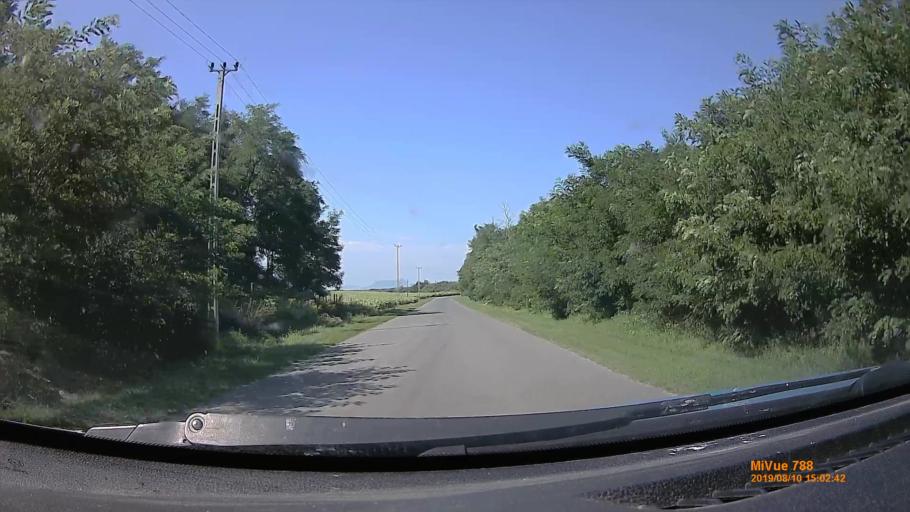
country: HU
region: Somogy
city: Lengyeltoti
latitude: 46.6579
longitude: 17.5743
